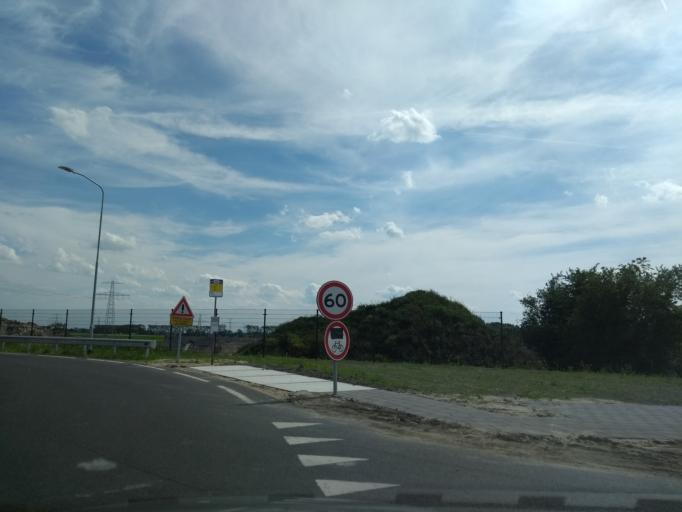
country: NL
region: Groningen
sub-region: Gemeente Zuidhorn
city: Aduard
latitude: 53.2600
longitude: 6.4691
